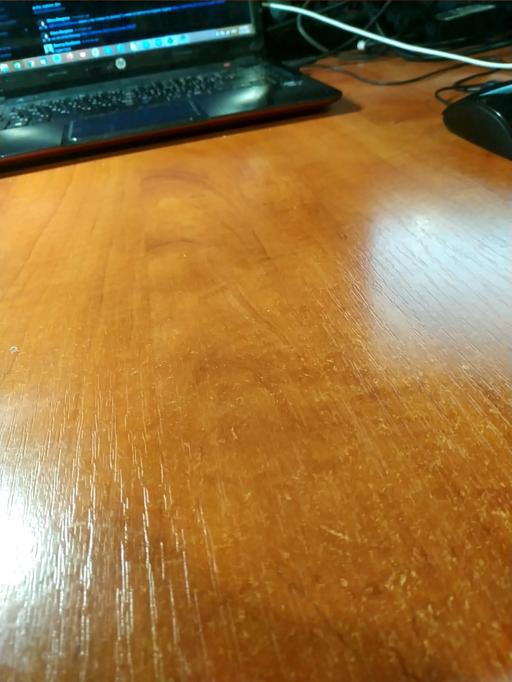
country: RU
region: Tverskaya
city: Vyshniy Volochek
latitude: 57.3568
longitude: 34.5784
